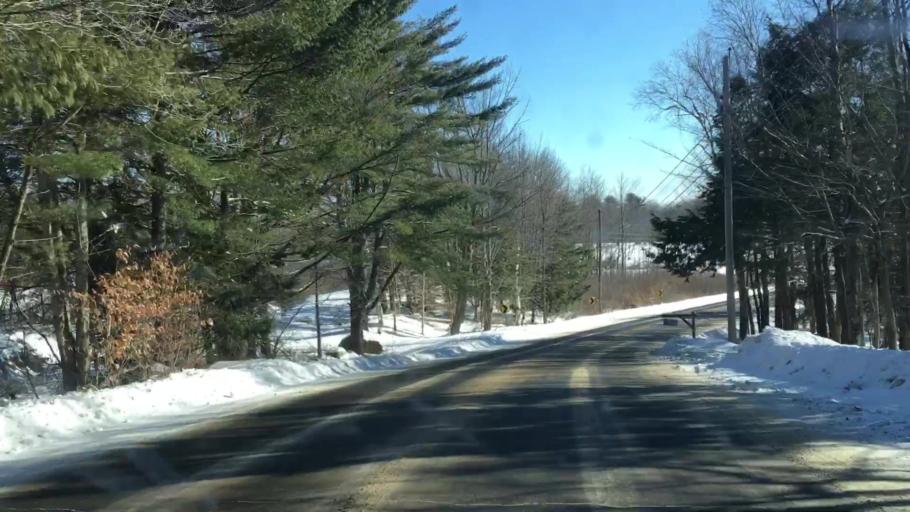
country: US
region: Maine
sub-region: Sagadahoc County
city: Topsham
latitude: 43.9101
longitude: -70.0136
